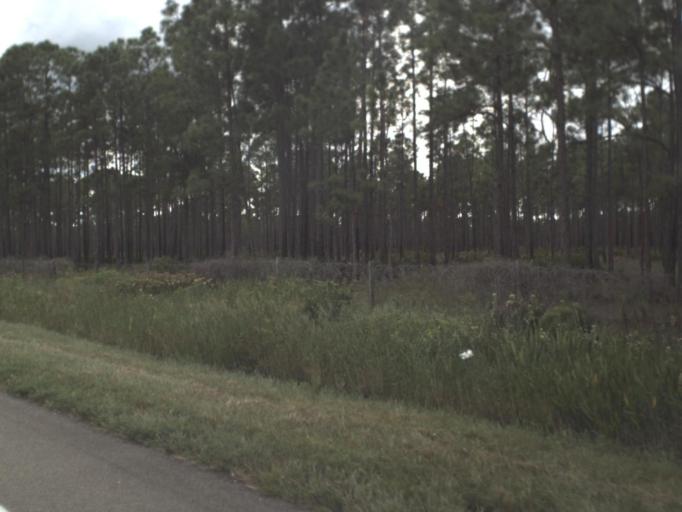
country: US
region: Florida
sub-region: Lee County
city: Olga
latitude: 26.8787
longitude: -81.7600
